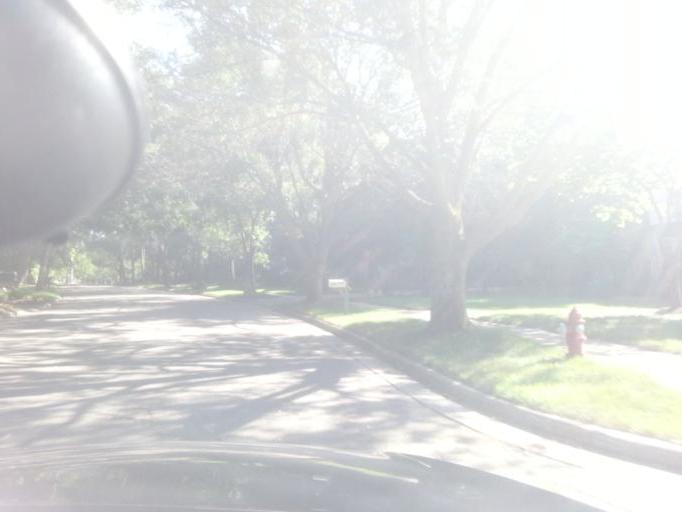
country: US
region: Wisconsin
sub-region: Dane County
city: Middleton
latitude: 43.0731
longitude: -89.4900
